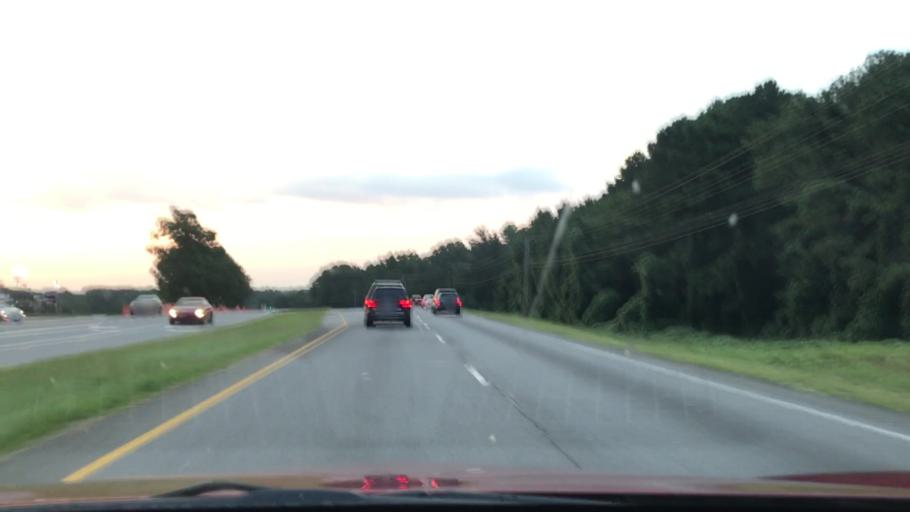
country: US
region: Georgia
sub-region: Gwinnett County
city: Lawrenceville
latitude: 34.0369
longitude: -83.9882
